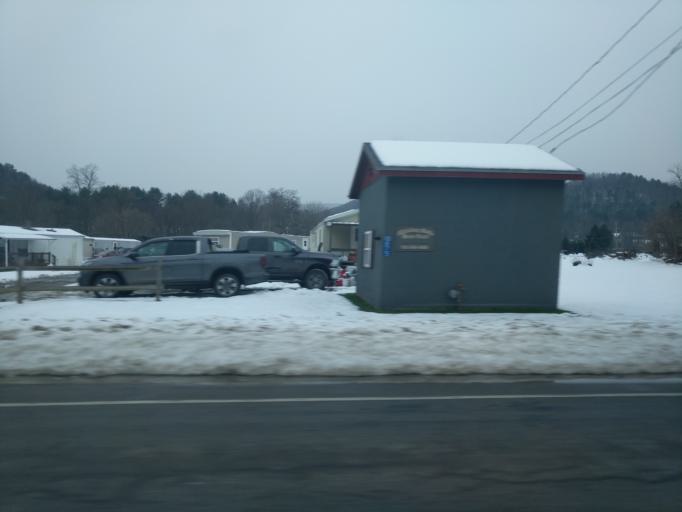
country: US
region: Pennsylvania
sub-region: Tioga County
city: Wellsboro
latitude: 41.8242
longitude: -77.2884
